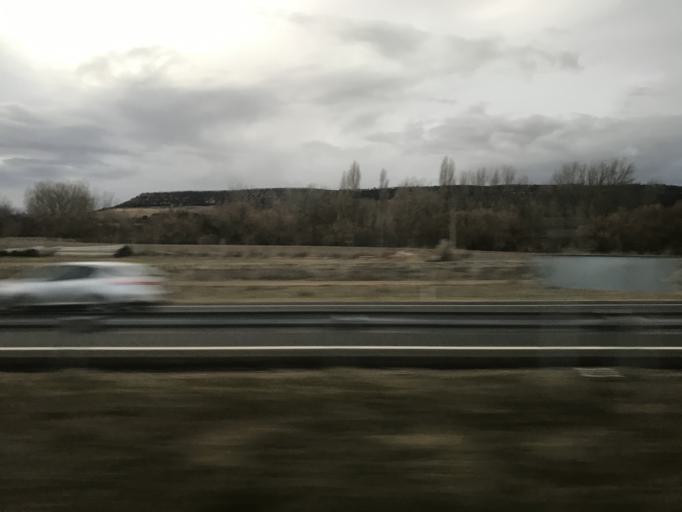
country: ES
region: Castille and Leon
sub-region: Provincia de Palencia
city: Quintana del Puente
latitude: 42.0742
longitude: -4.2137
